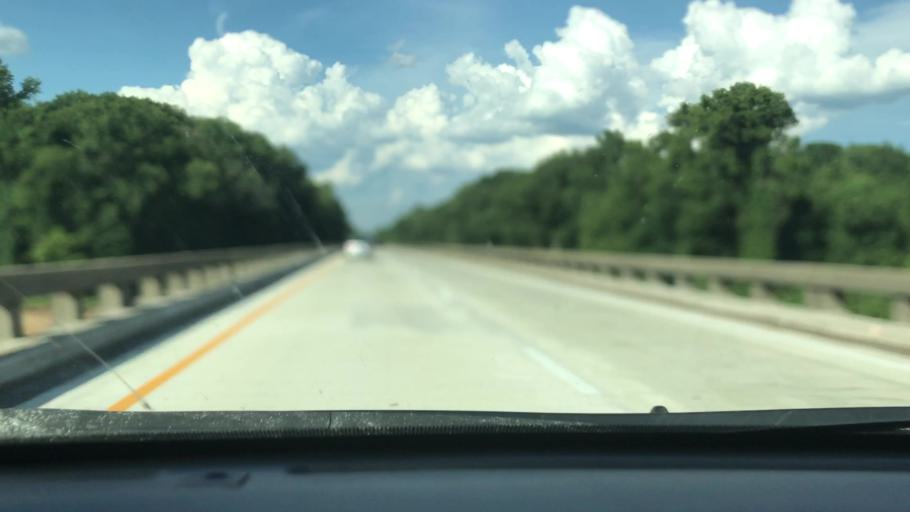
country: US
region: South Carolina
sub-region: Florence County
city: Florence
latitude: 34.2991
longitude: -79.6343
